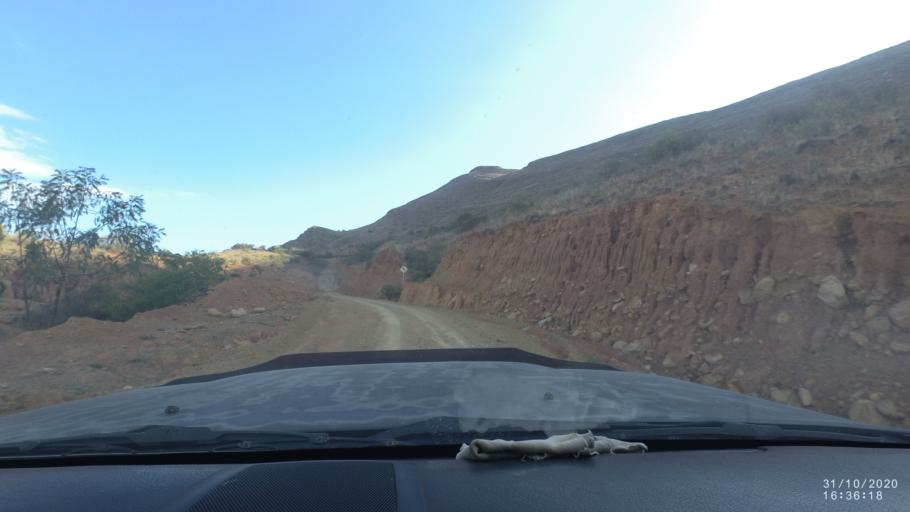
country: BO
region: Chuquisaca
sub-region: Provincia Zudanez
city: Mojocoya
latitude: -18.4587
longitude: -64.5829
